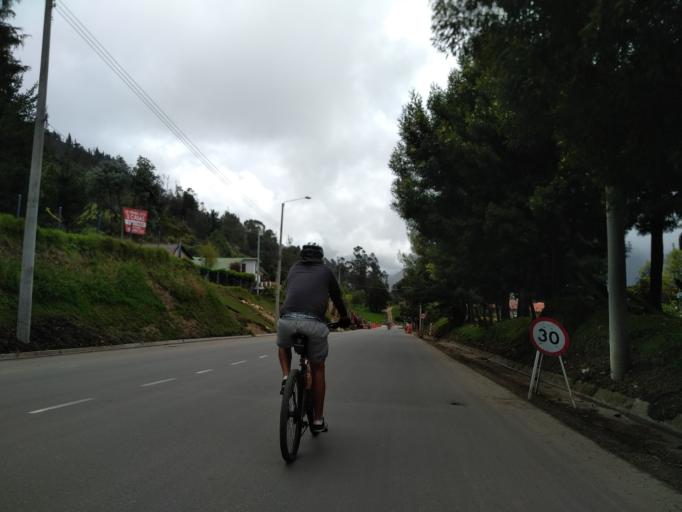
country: CO
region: Bogota D.C.
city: Barrio San Luis
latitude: 4.6649
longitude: -74.0025
